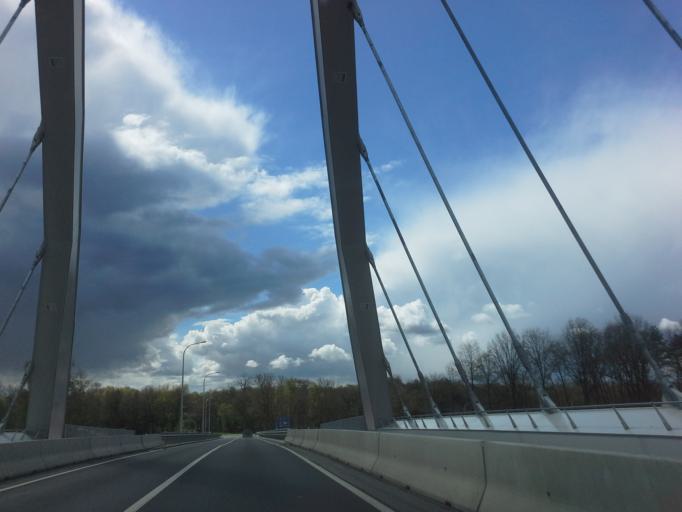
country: BE
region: Flanders
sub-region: Provincie Antwerpen
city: Meerhout
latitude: 51.1074
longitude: 5.0531
